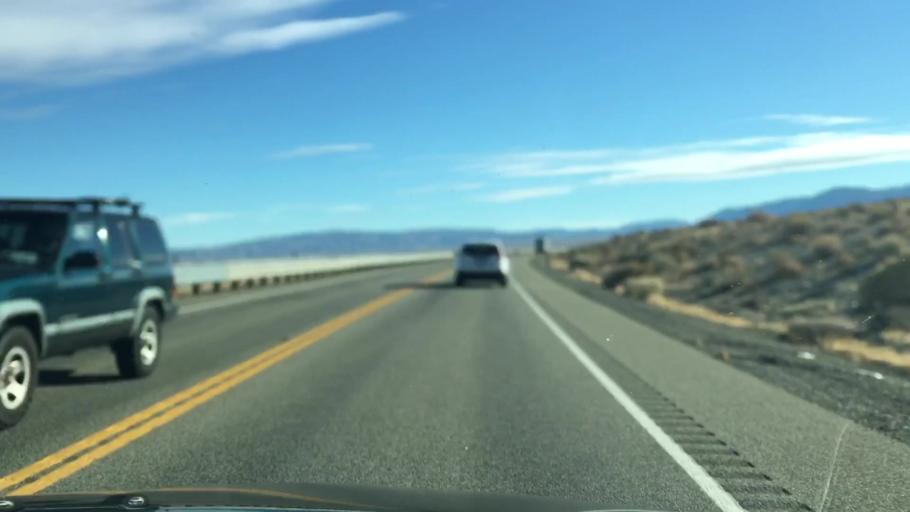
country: US
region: Nevada
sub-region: Mineral County
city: Hawthorne
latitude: 38.6083
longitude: -118.7140
